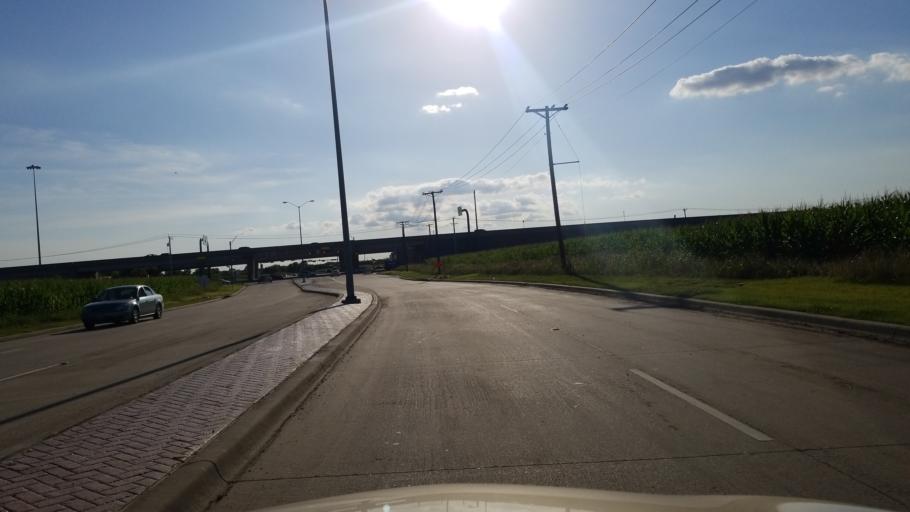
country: US
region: Texas
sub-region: Dallas County
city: Grand Prairie
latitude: 32.6816
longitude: -97.0214
